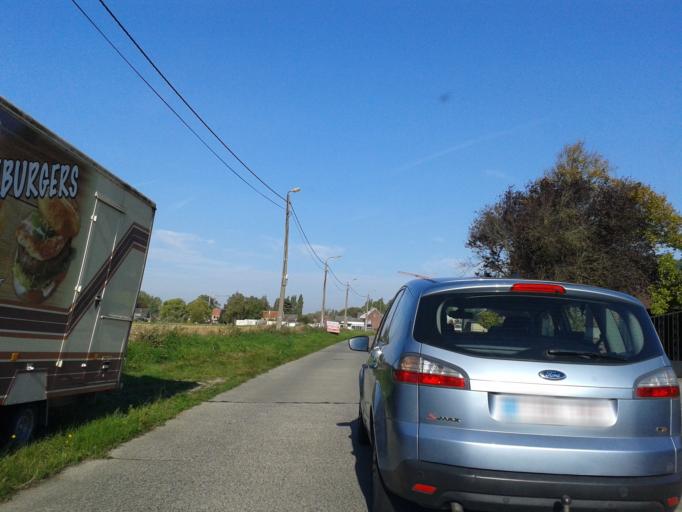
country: BE
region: Flanders
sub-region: Provincie Oost-Vlaanderen
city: Aalst
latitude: 50.9730
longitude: 4.0814
